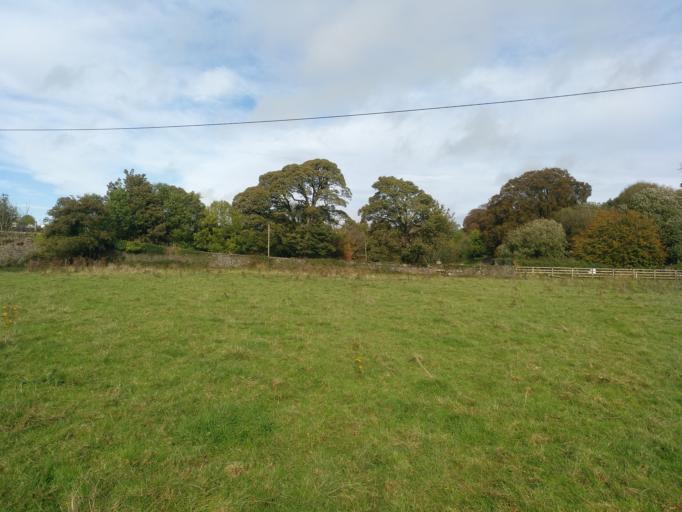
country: IE
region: Leinster
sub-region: Kilkenny
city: Castlecomer
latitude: 52.7948
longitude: -7.2079
